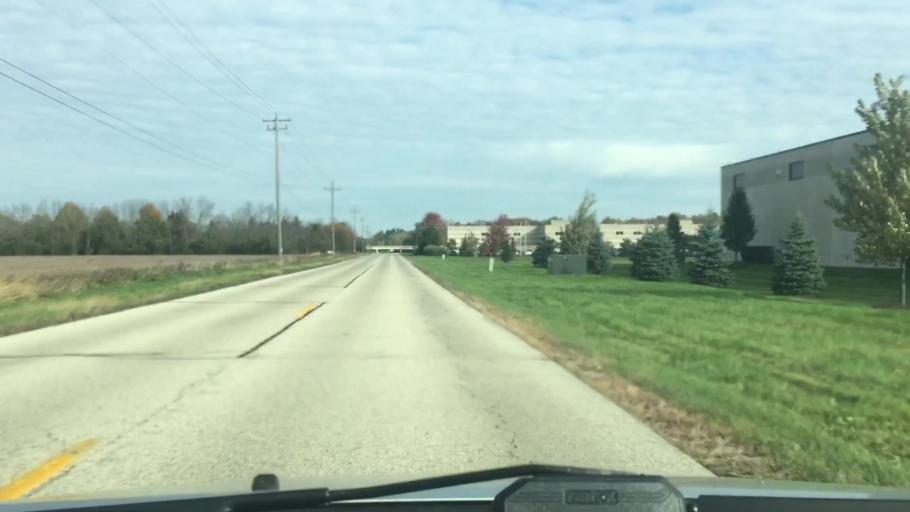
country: US
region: Wisconsin
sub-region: Waukesha County
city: Dousman
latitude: 43.0640
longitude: -88.4813
